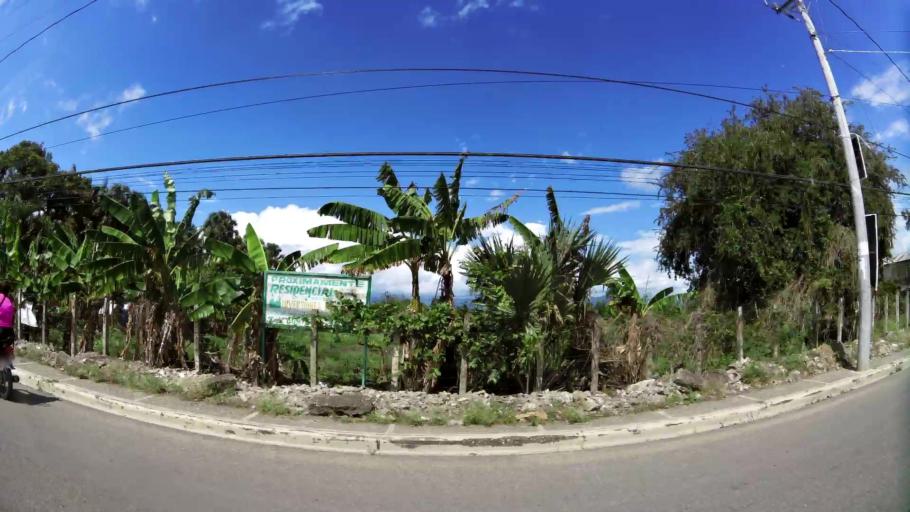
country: DO
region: Santiago
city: Licey al Medio
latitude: 19.3812
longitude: -70.6176
